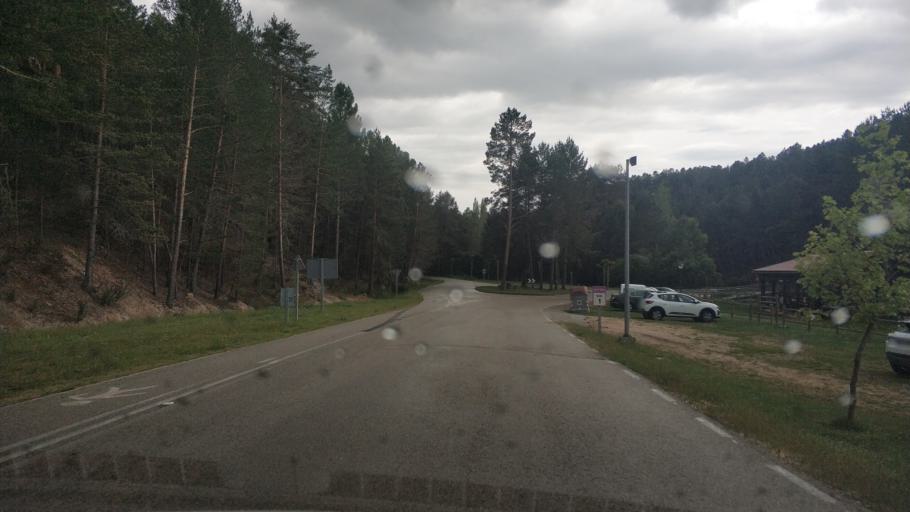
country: ES
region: Castille and Leon
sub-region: Provincia de Soria
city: San Leonardo de Yague
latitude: 41.8380
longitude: -3.0652
